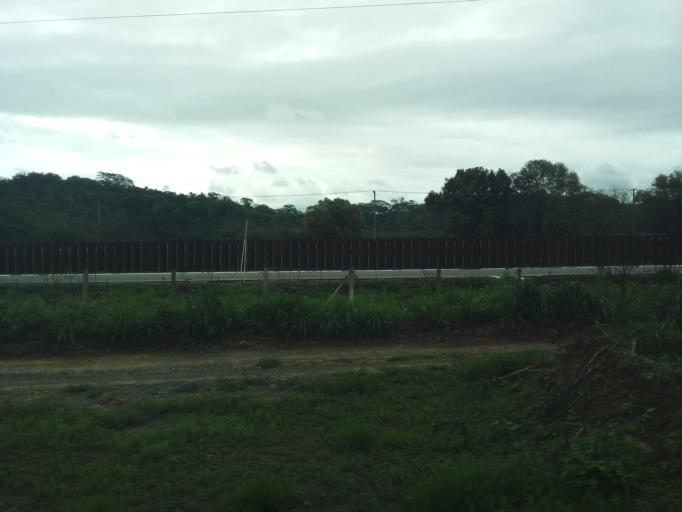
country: BR
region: Minas Gerais
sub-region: Ipatinga
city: Ipatinga
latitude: -19.4795
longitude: -42.4899
